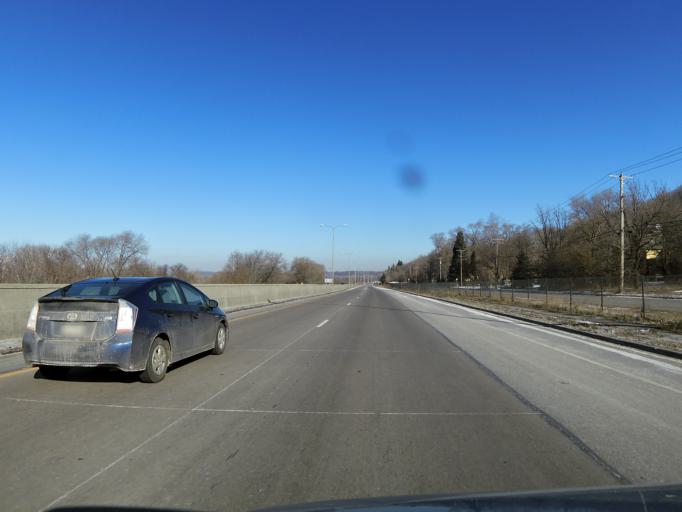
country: US
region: Minnesota
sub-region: Dakota County
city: South Saint Paul
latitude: 44.9034
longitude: -93.0104
